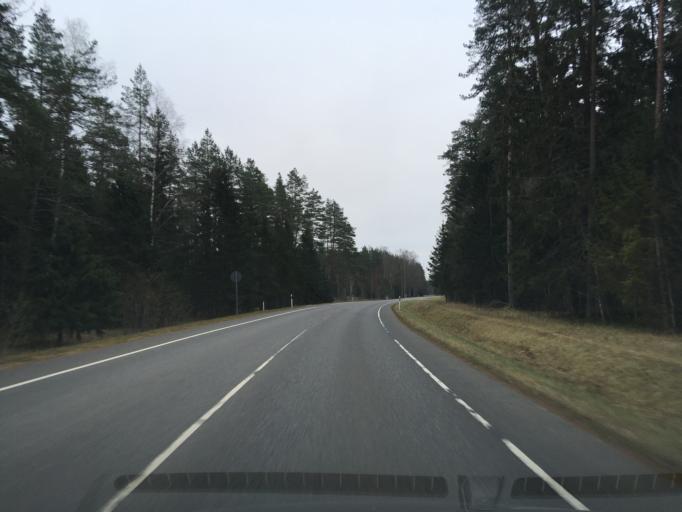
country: EE
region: Laeaene-Virumaa
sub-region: Kadrina vald
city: Kadrina
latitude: 59.4557
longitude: 26.0172
